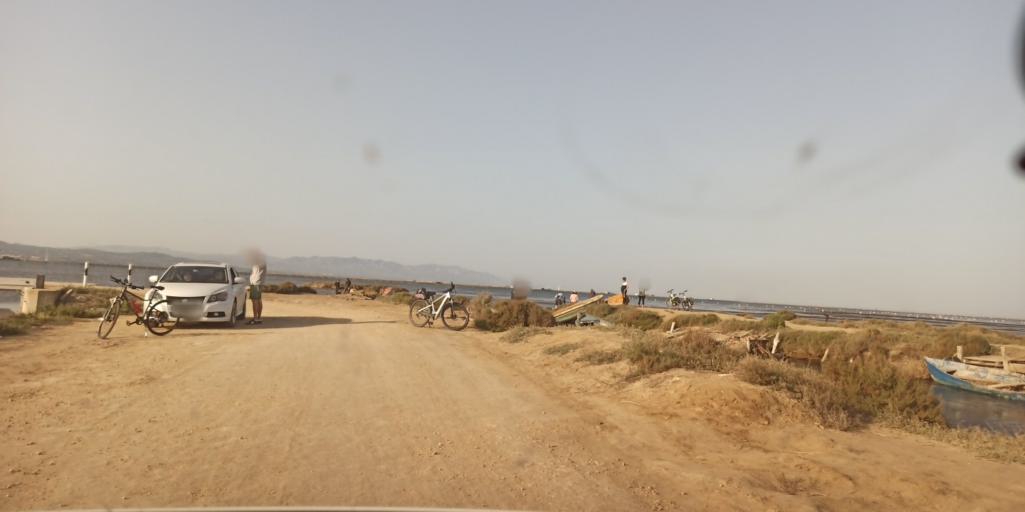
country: ES
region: Catalonia
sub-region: Provincia de Tarragona
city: Deltebre
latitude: 40.7639
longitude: 0.7499
